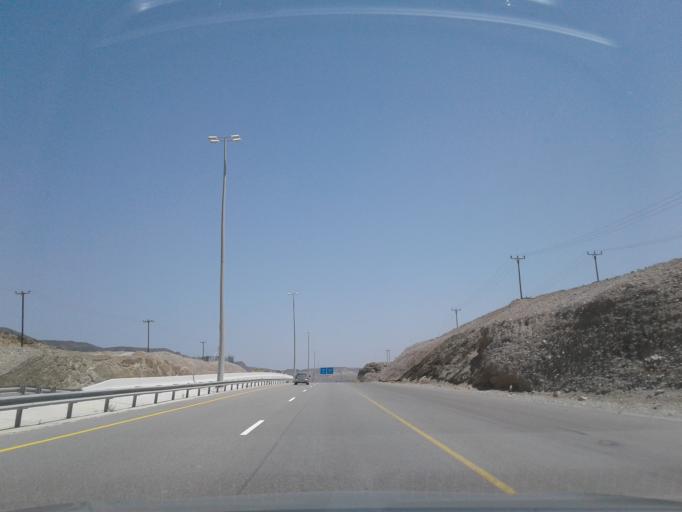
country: OM
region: Muhafazat Masqat
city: Muscat
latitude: 23.2568
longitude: 58.7742
